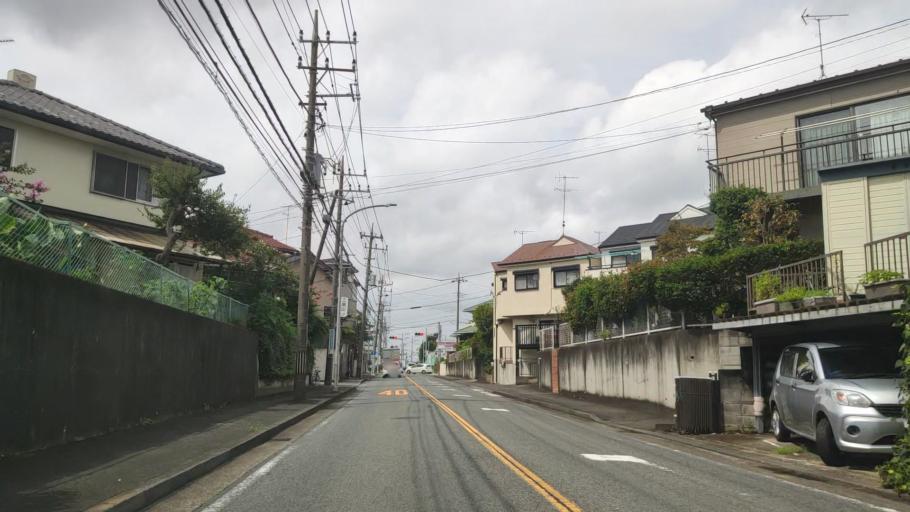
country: JP
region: Kanagawa
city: Minami-rinkan
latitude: 35.4712
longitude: 139.4908
